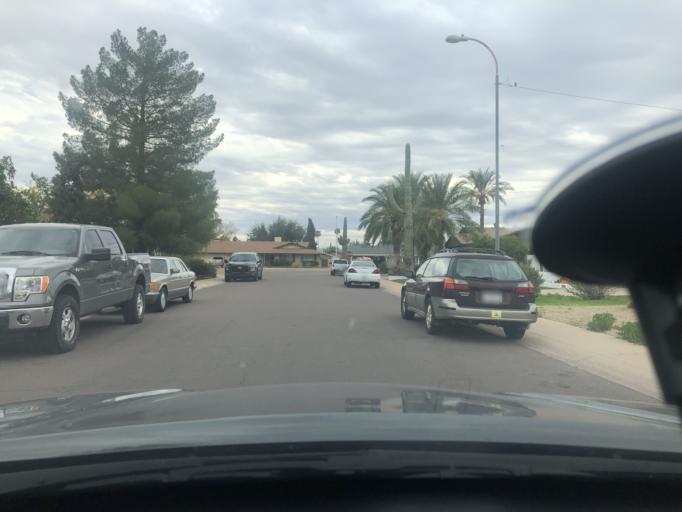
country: US
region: Arizona
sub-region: Maricopa County
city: Scottsdale
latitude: 33.4884
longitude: -111.8977
